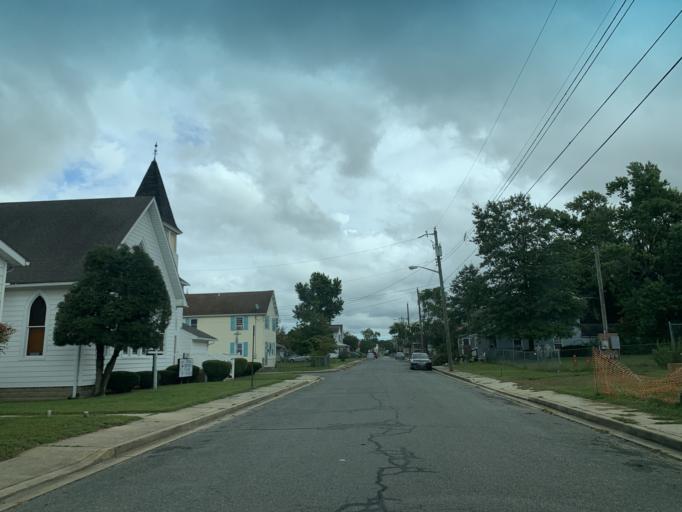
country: US
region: Maryland
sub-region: Caroline County
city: Denton
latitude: 38.8872
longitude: -75.8283
